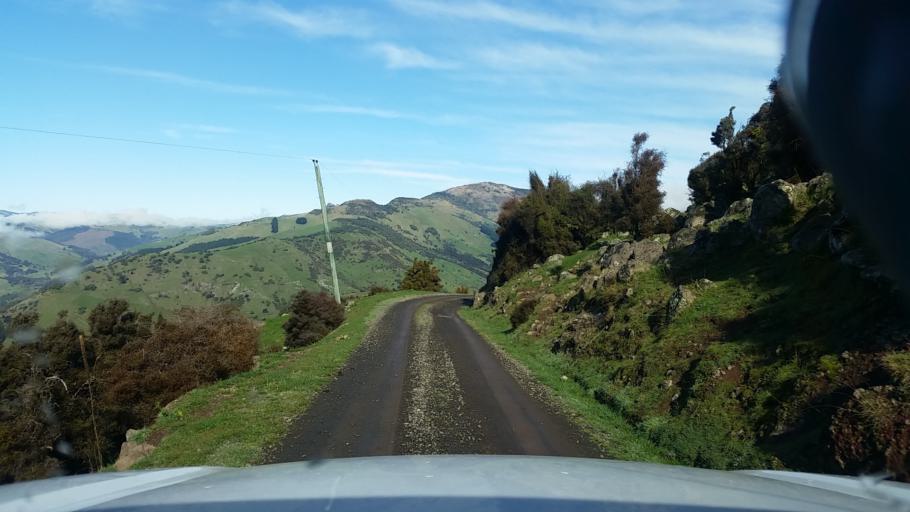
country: NZ
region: Canterbury
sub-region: Christchurch City
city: Christchurch
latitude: -43.6608
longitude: 172.8768
